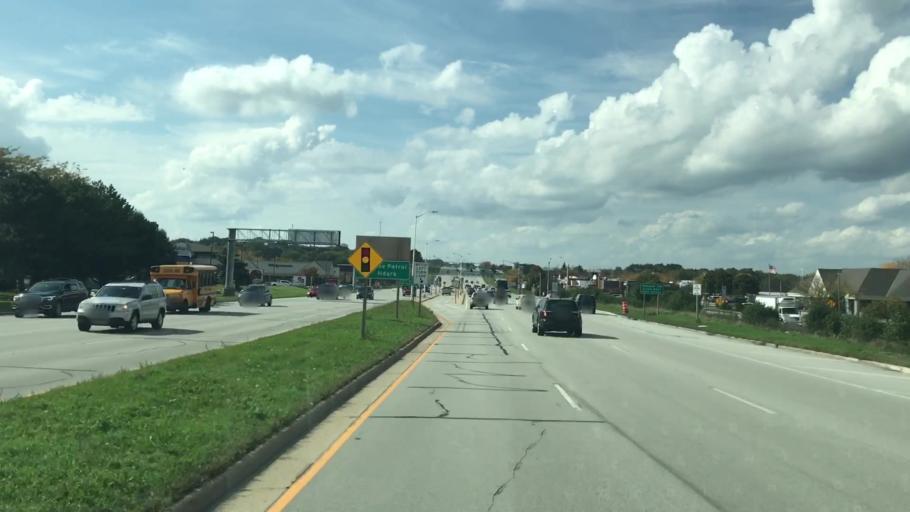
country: US
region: Wisconsin
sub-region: Waukesha County
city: Waukesha
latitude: 43.0331
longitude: -88.1754
